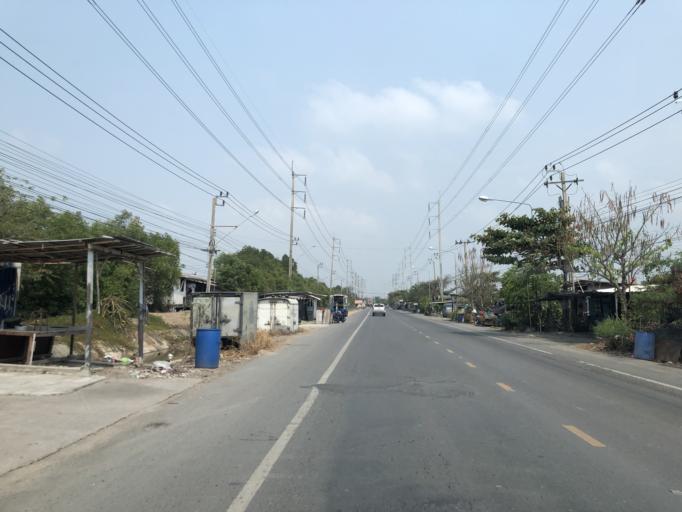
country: TH
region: Samut Prakan
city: Bang Bo
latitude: 13.5146
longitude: 100.8330
